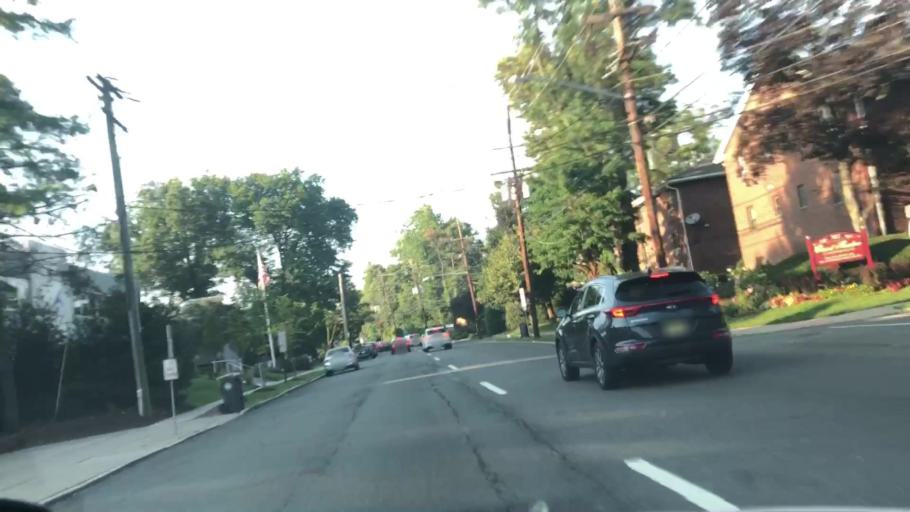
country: US
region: New Jersey
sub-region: Bergen County
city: Englewood
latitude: 40.8824
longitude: -73.9780
